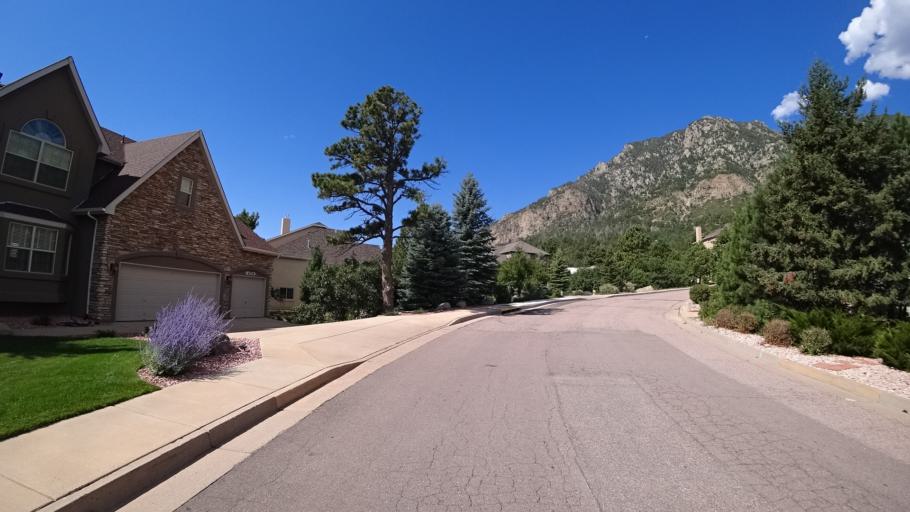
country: US
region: Colorado
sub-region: El Paso County
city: Fort Carson
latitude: 38.7412
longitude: -104.8365
